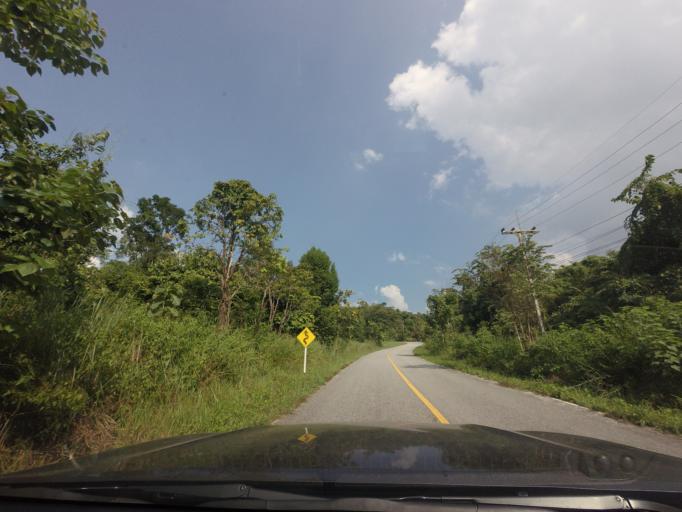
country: TH
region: Phitsanulok
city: Nakhon Thai
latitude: 17.0209
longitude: 100.9691
